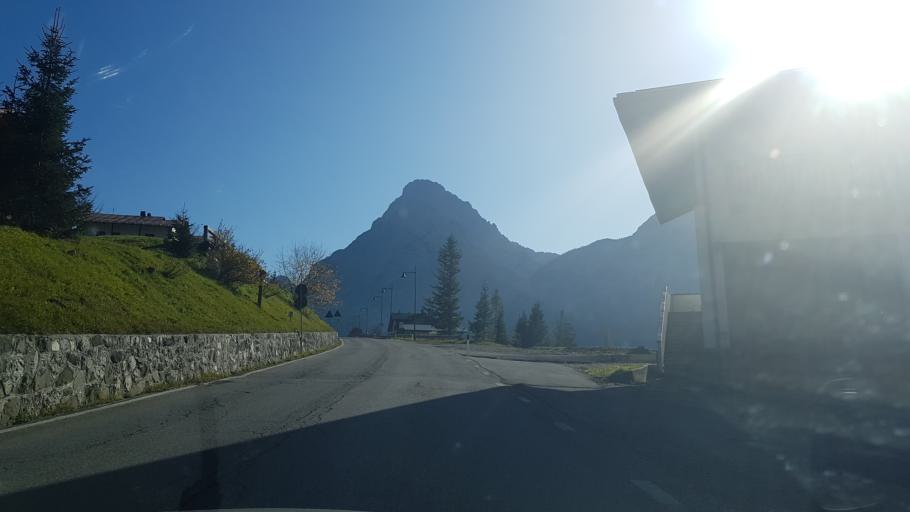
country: IT
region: Veneto
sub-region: Provincia di Belluno
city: Sappada
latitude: 46.5666
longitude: 12.6643
